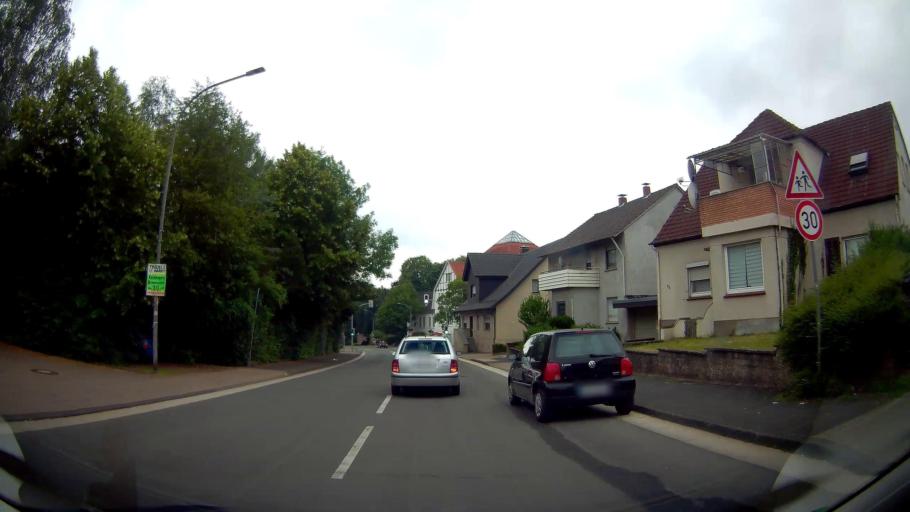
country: DE
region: North Rhine-Westphalia
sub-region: Regierungsbezirk Detmold
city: Kirchlengern
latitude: 52.2009
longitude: 8.6409
